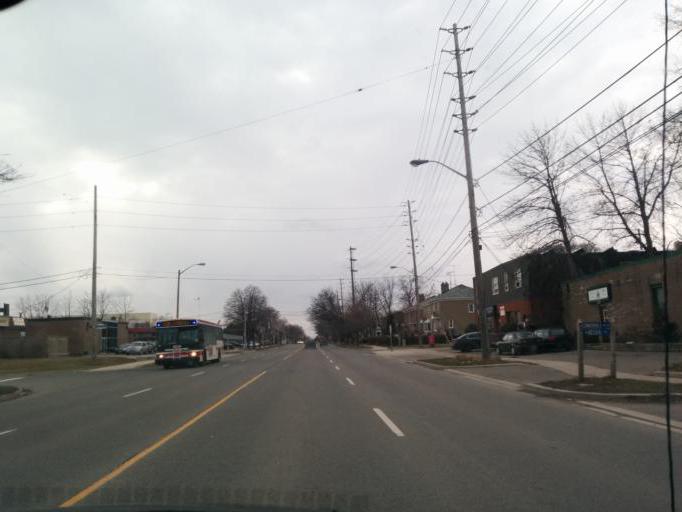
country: CA
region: Ontario
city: Etobicoke
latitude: 43.6056
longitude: -79.5281
